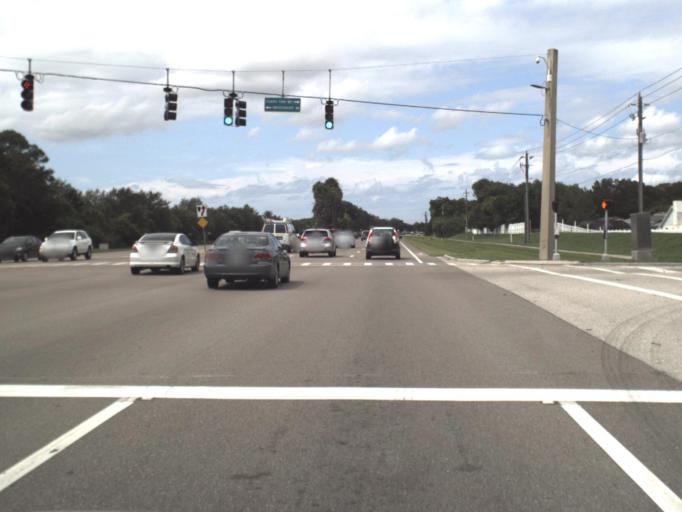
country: US
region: Florida
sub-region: Sarasota County
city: Desoto Lakes
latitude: 27.3886
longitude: -82.4959
